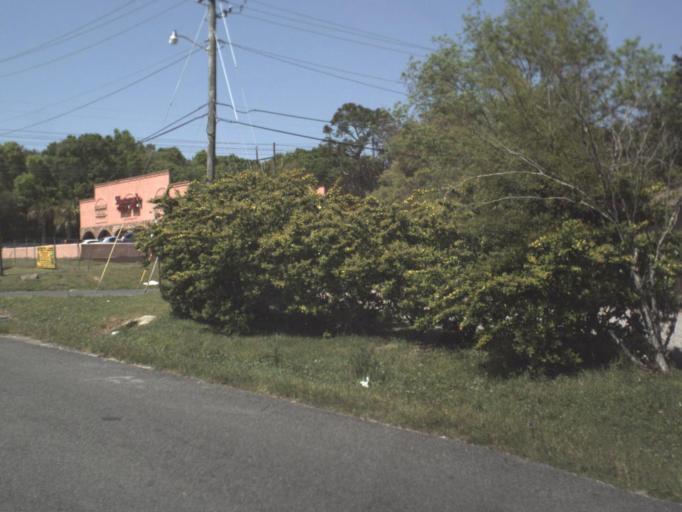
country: US
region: Florida
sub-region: Escambia County
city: West Pensacola
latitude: 30.4492
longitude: -87.2912
